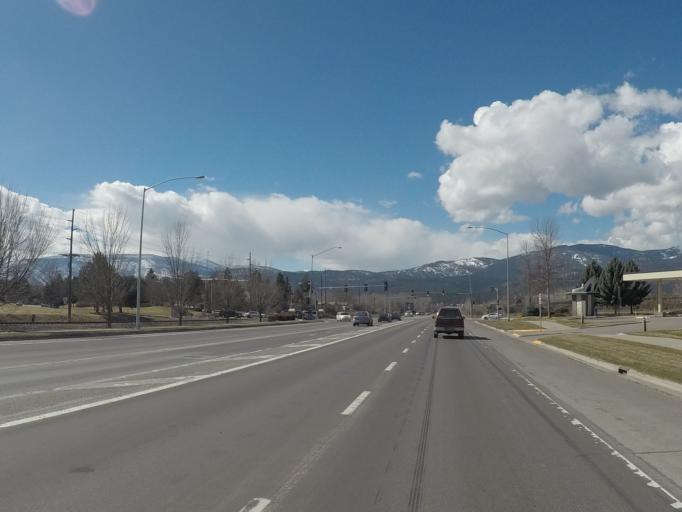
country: US
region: Montana
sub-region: Missoula County
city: Orchard Homes
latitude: 46.8334
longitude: -114.0487
